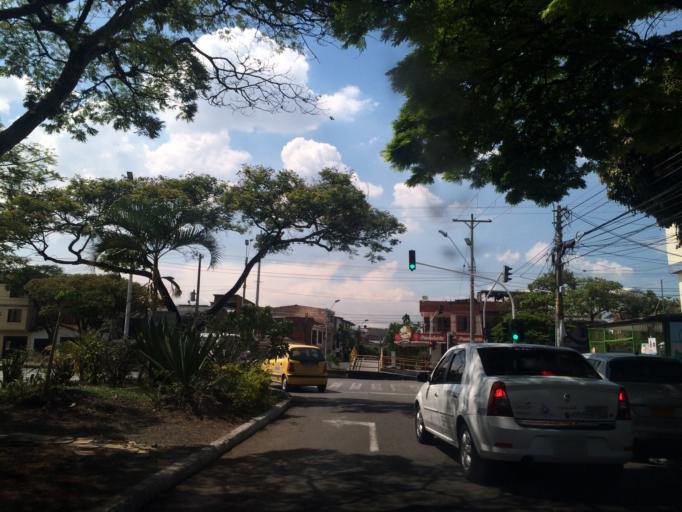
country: CO
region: Valle del Cauca
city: Cali
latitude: 3.4182
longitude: -76.5247
